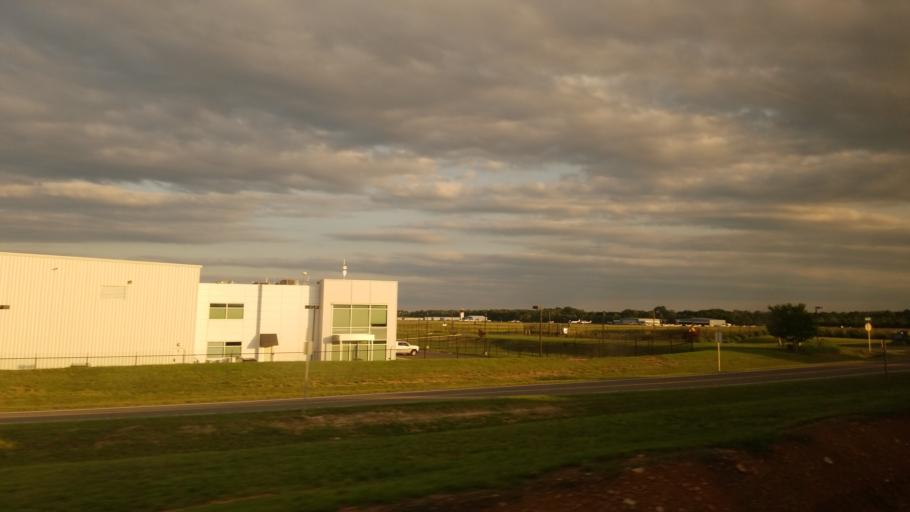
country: US
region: Virginia
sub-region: City of Manassas
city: Manassas
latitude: 38.7334
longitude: -77.5194
